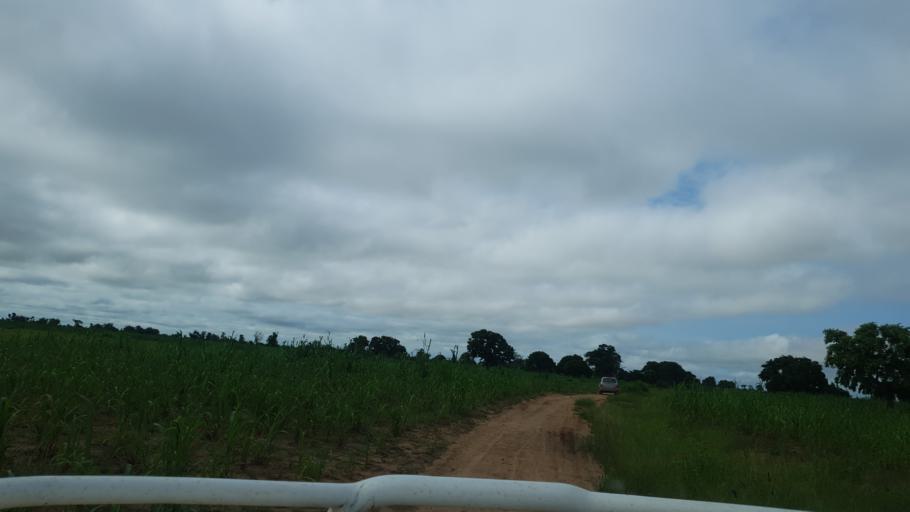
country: ML
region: Segou
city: Baroueli
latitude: 13.4939
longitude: -6.8963
